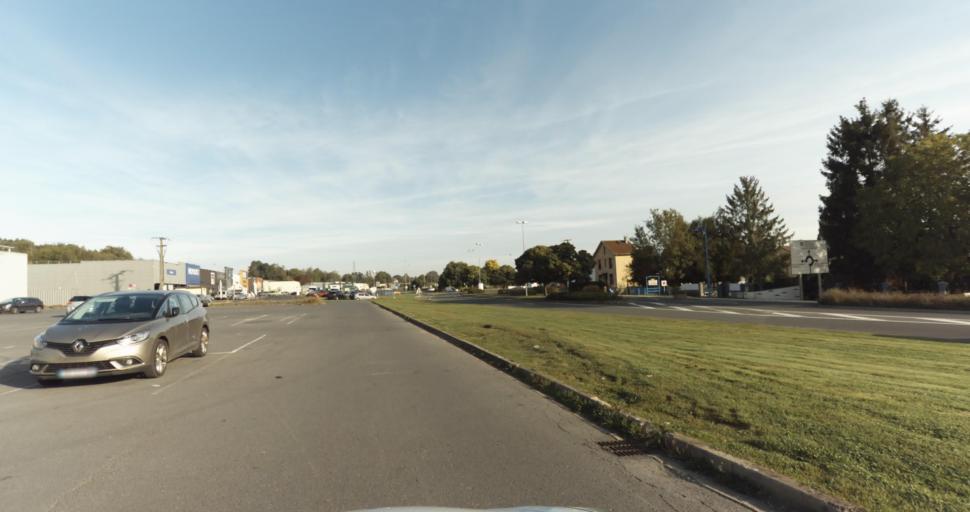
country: FR
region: Champagne-Ardenne
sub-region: Departement des Ardennes
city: Villers-Semeuse
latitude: 49.7307
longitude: 4.7528
